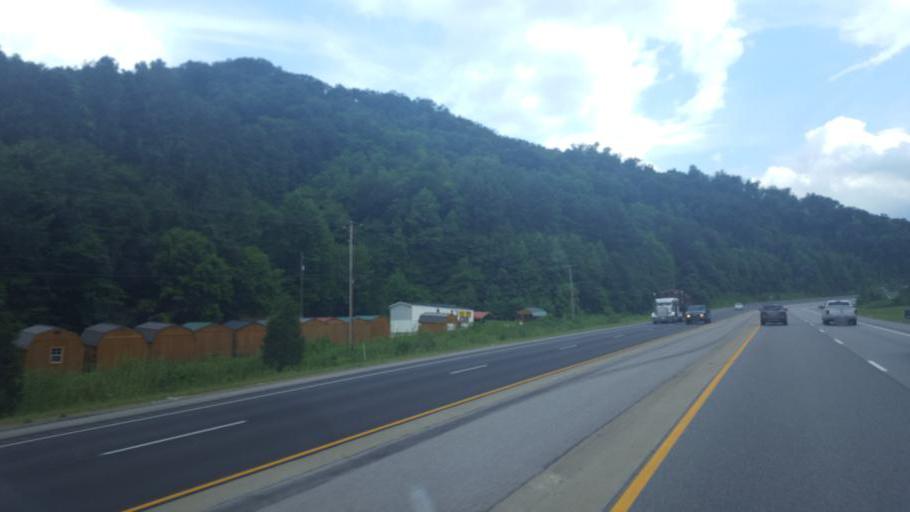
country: US
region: Kentucky
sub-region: Pike County
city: Pikeville
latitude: 37.4223
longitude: -82.5169
